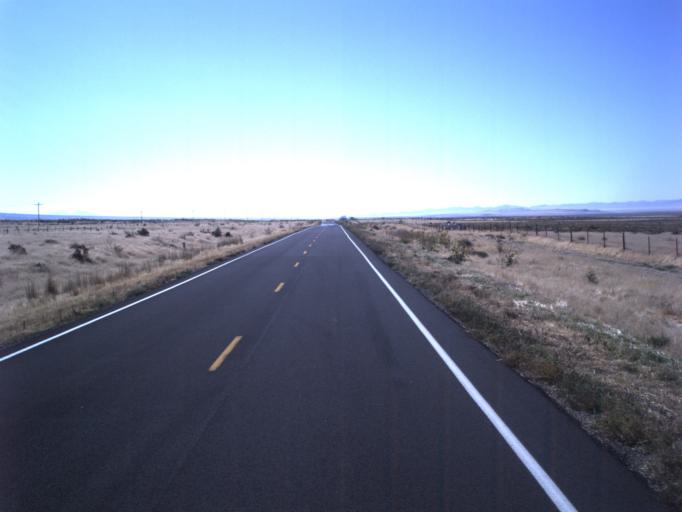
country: US
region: Utah
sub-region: Tooele County
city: Grantsville
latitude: 40.5210
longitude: -112.7477
